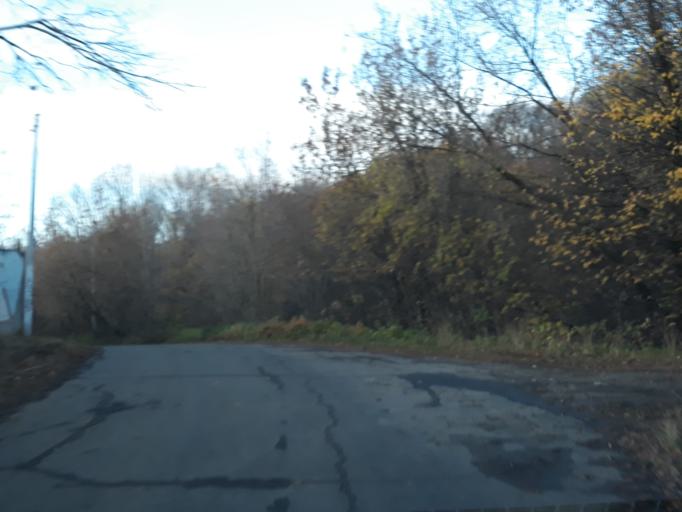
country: RU
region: Nizjnij Novgorod
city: Nizhniy Novgorod
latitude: 56.2819
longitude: 43.9701
